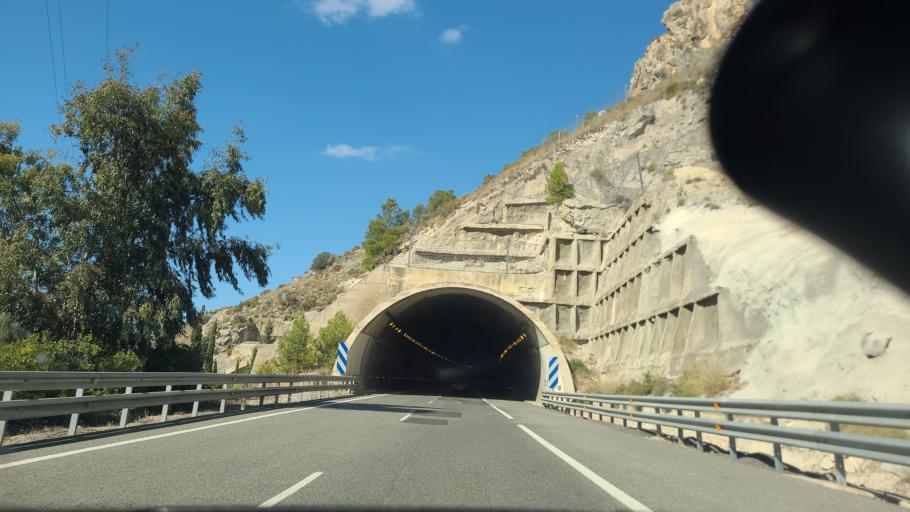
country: ES
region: Andalusia
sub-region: Provincia de Jaen
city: Pegalajar
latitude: 37.6894
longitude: -3.6300
